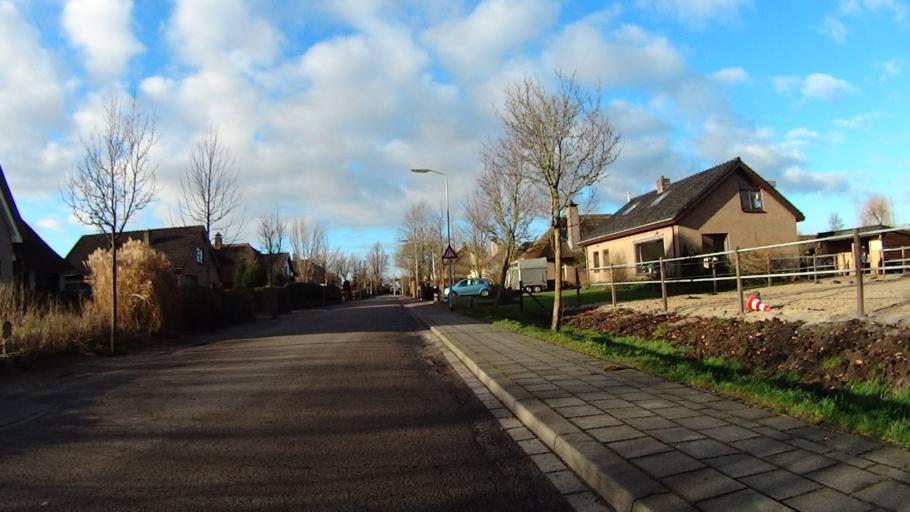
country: NL
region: Gelderland
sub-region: Gemeente Barneveld
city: Zwartebroek
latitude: 52.1792
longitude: 5.5028
